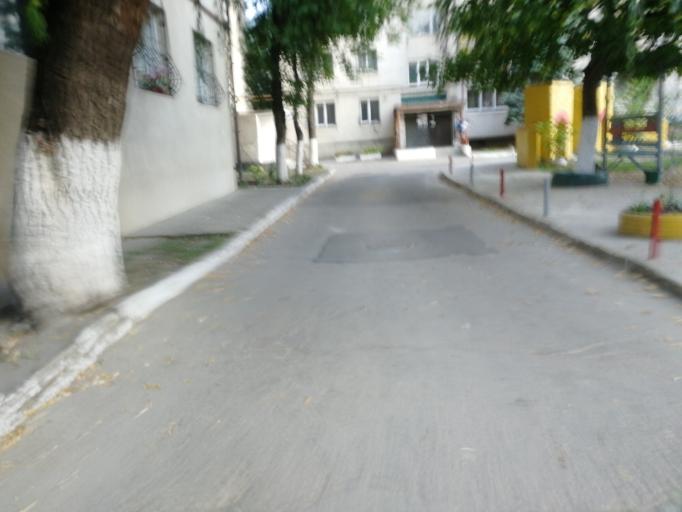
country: MD
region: Chisinau
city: Chisinau
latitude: 47.0253
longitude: 28.8750
